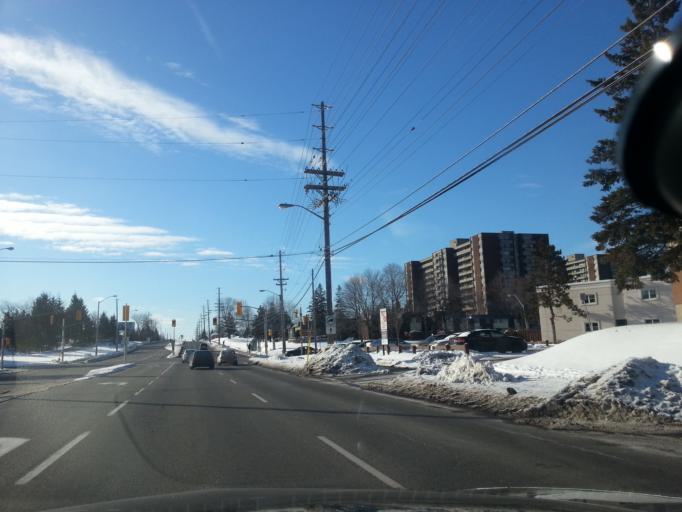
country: CA
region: Ontario
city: Ottawa
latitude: 45.3880
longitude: -75.6199
